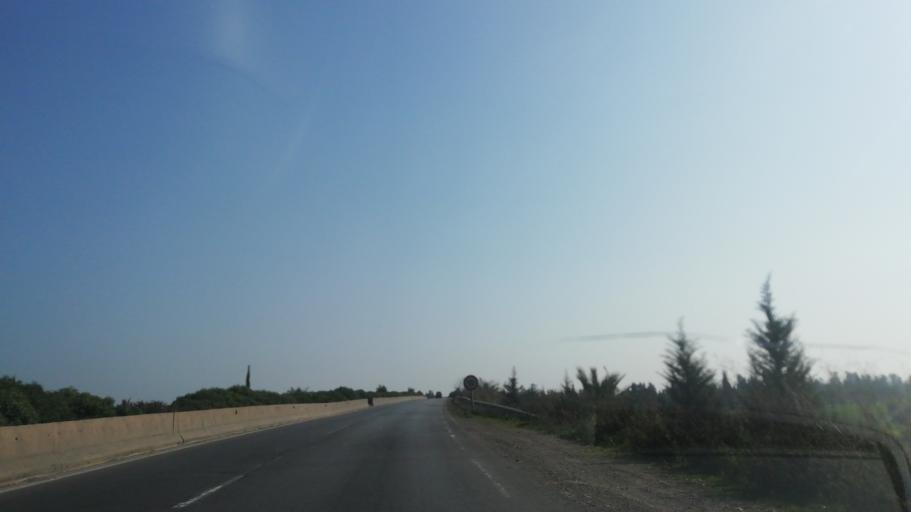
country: DZ
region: Oran
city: Bou Tlelis
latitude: 35.5677
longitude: -0.9087
